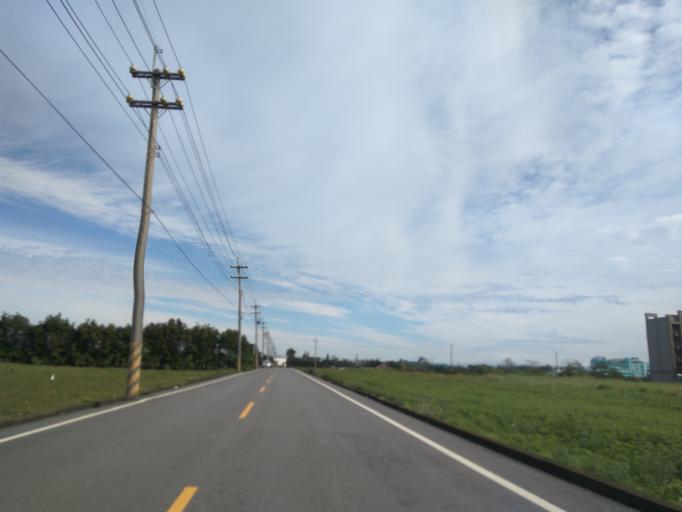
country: TW
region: Taiwan
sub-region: Hsinchu
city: Zhubei
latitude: 24.9903
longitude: 121.0903
